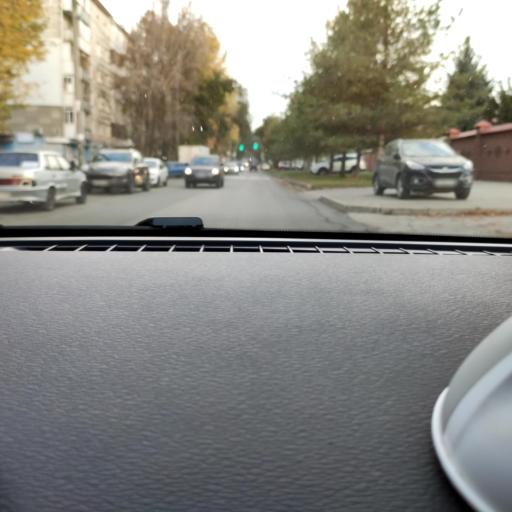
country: RU
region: Samara
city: Samara
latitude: 53.2098
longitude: 50.2377
